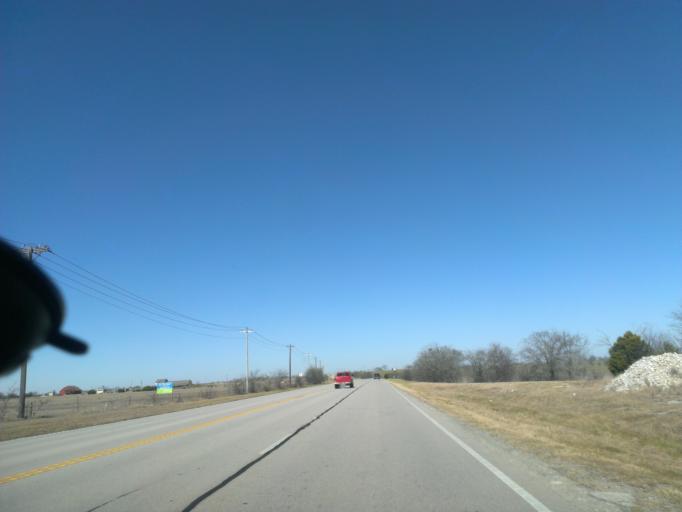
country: US
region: Texas
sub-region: Williamson County
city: Florence
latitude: 30.8442
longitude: -97.9051
